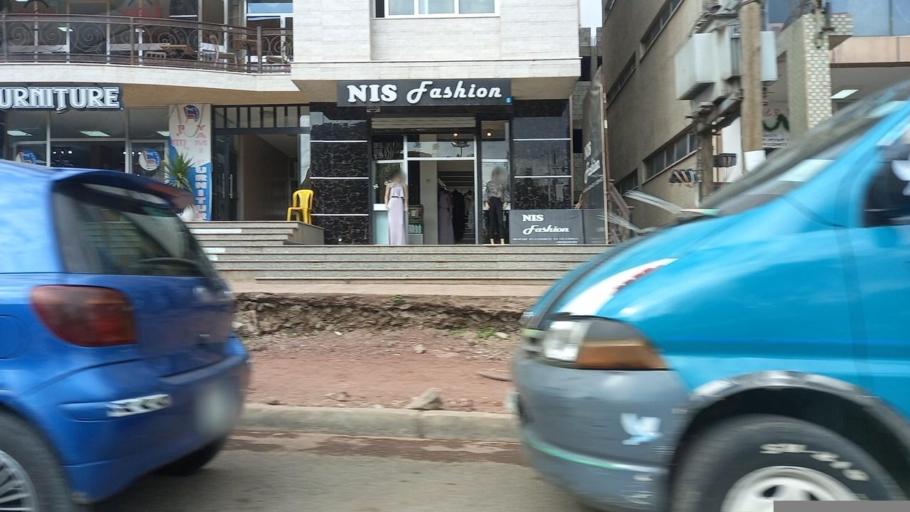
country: ET
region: Adis Abeba
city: Addis Ababa
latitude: 9.0102
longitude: 38.8495
